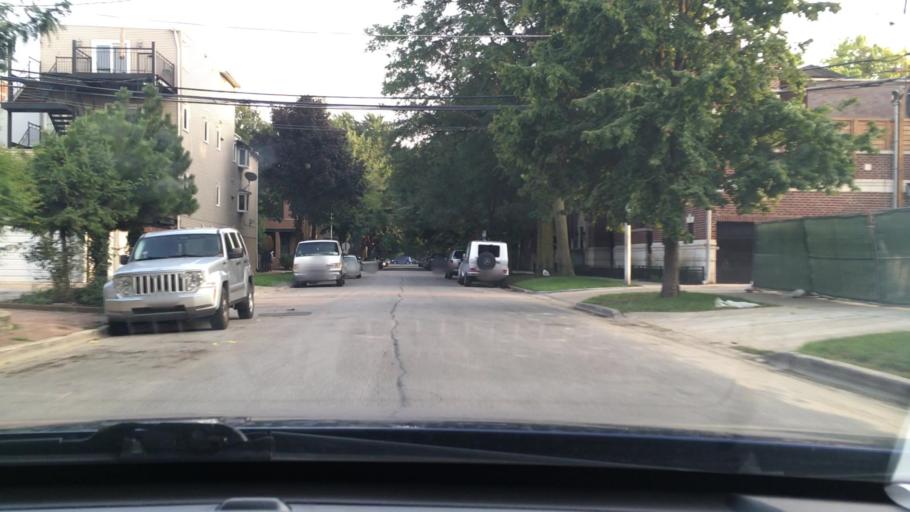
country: US
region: Illinois
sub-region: Cook County
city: Chicago
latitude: 41.9340
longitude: -87.6660
